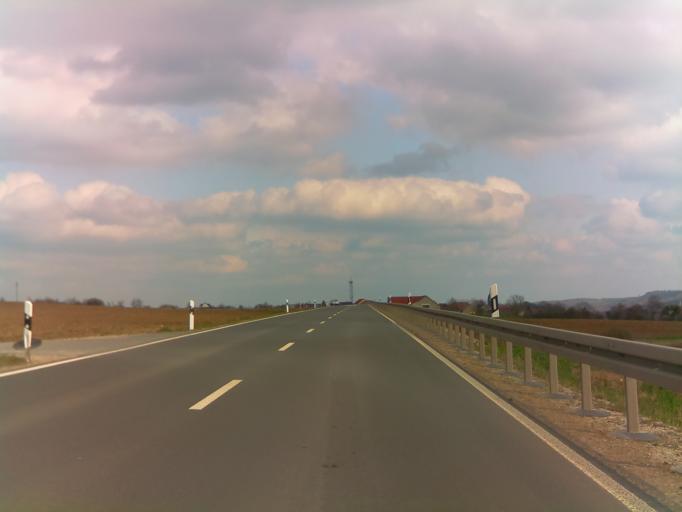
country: DE
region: Thuringia
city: Milda
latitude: 50.8759
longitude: 11.4731
